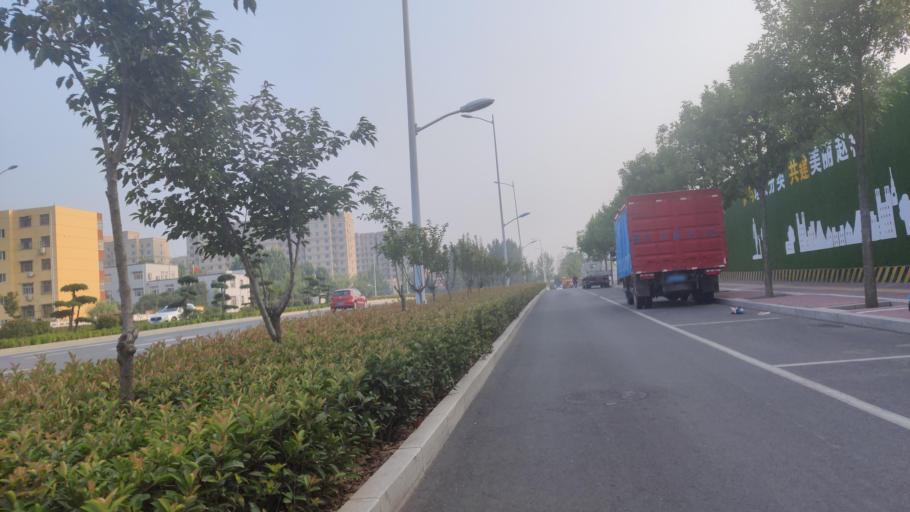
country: CN
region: Henan Sheng
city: Zhongyuanlu
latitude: 35.7585
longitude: 115.0829
